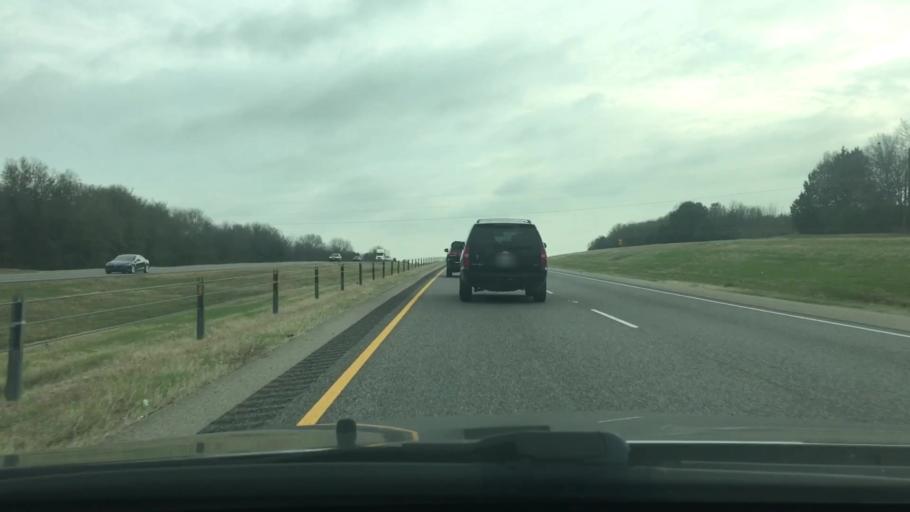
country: US
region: Texas
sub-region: Freestone County
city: Fairfield
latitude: 31.6428
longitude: -96.1589
